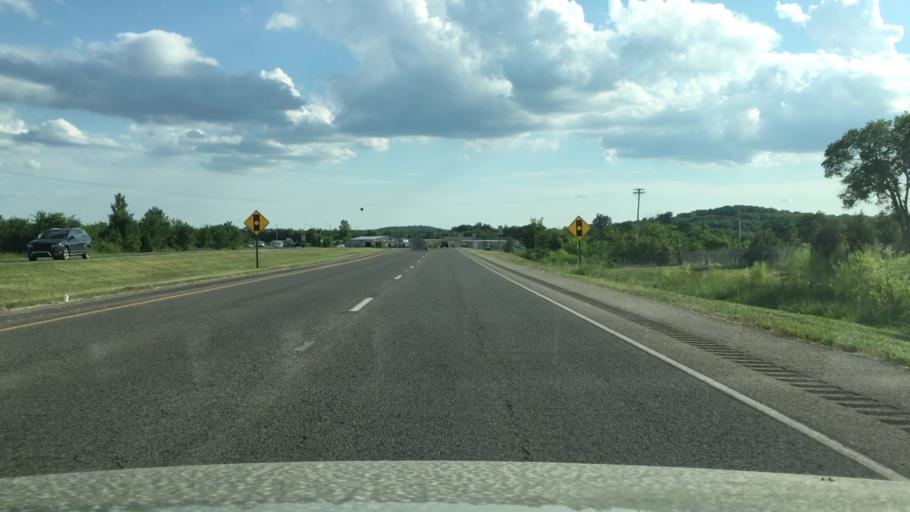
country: US
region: Oklahoma
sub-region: Cherokee County
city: Tahlequah
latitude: 35.9234
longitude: -95.0025
